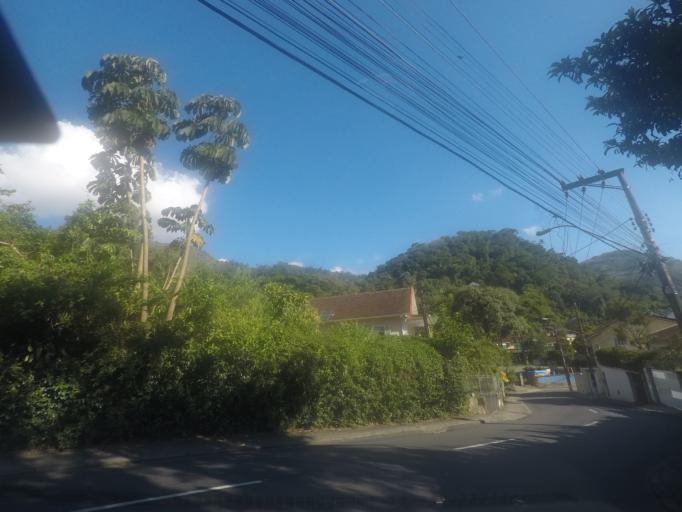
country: BR
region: Rio de Janeiro
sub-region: Petropolis
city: Petropolis
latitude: -22.5140
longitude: -43.1679
